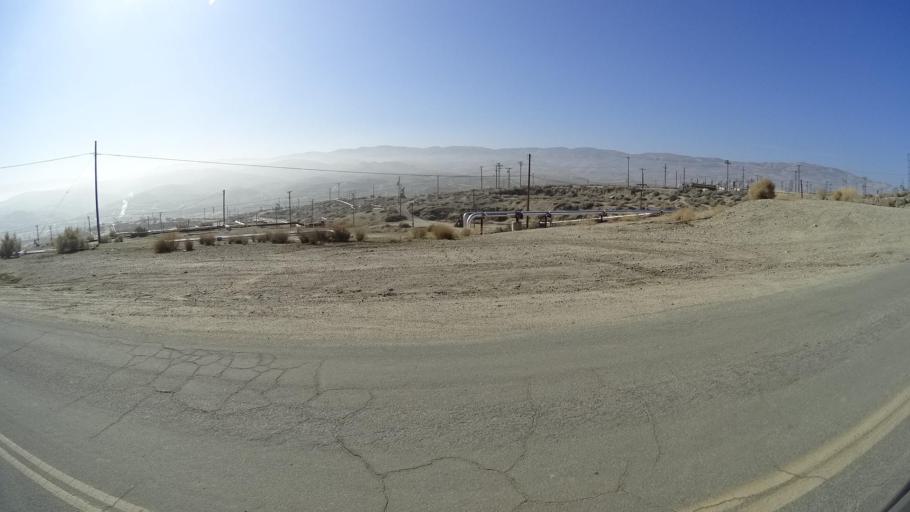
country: US
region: California
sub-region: Kern County
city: Taft Heights
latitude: 35.1144
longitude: -119.4666
